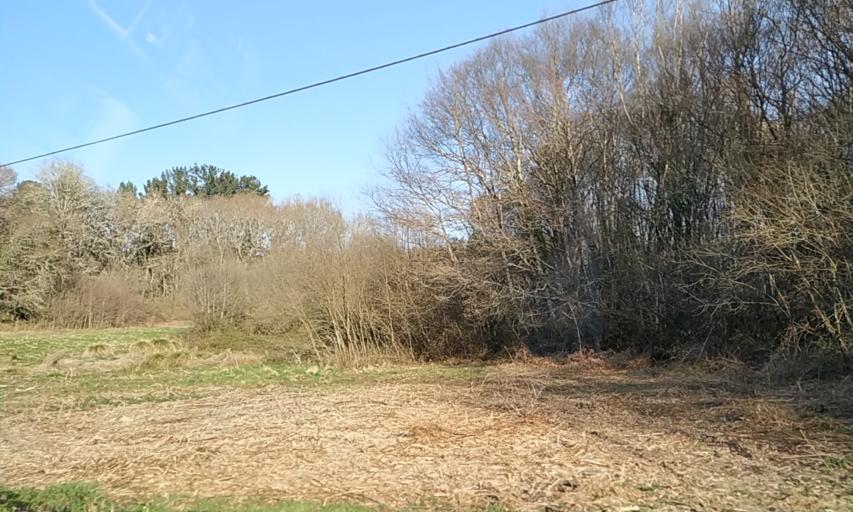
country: ES
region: Galicia
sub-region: Provincia de Lugo
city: Corgo
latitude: 42.9391
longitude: -7.4434
